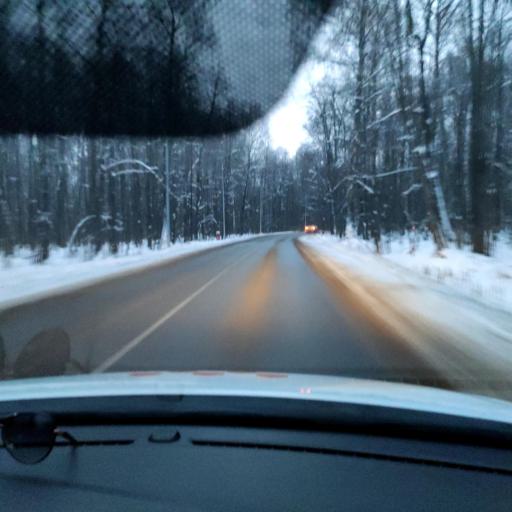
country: RU
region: Tatarstan
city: Vysokaya Gora
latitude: 55.9313
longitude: 49.1912
